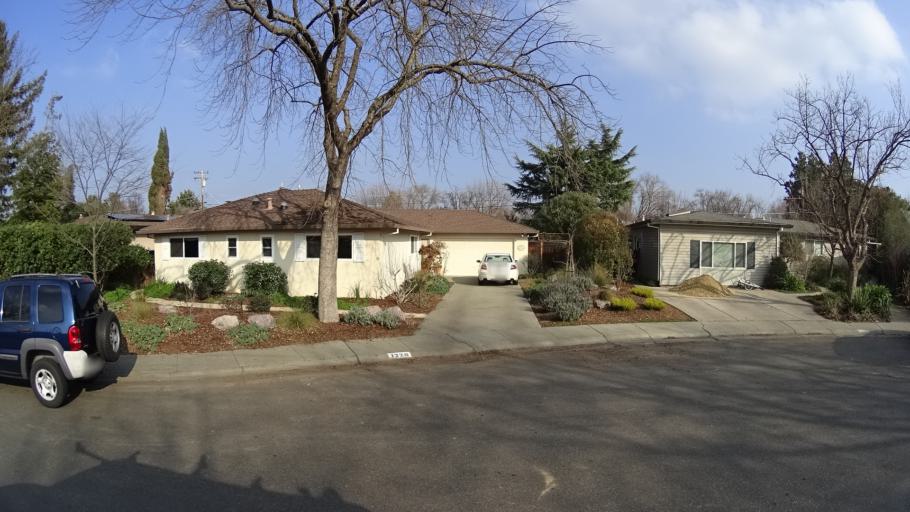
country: US
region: California
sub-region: Yolo County
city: Davis
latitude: 38.5558
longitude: -121.7441
